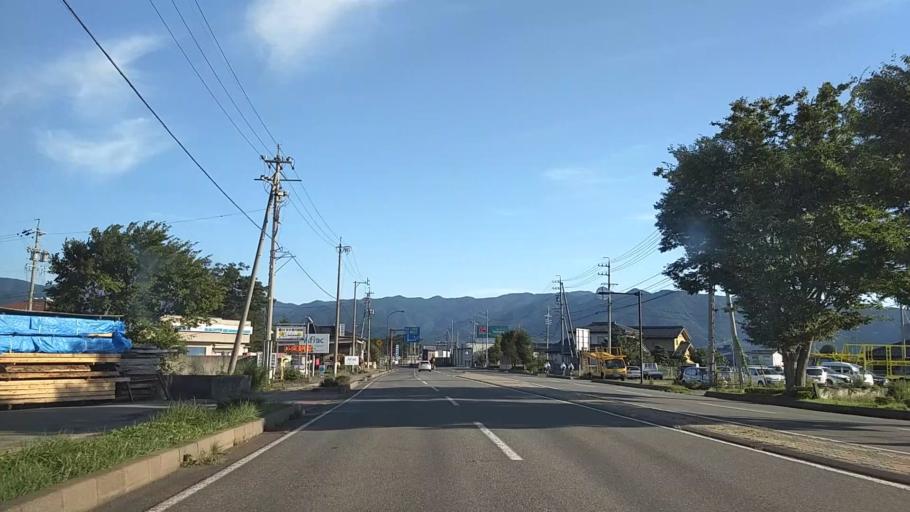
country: JP
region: Nagano
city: Nagano-shi
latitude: 36.5869
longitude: 138.1880
